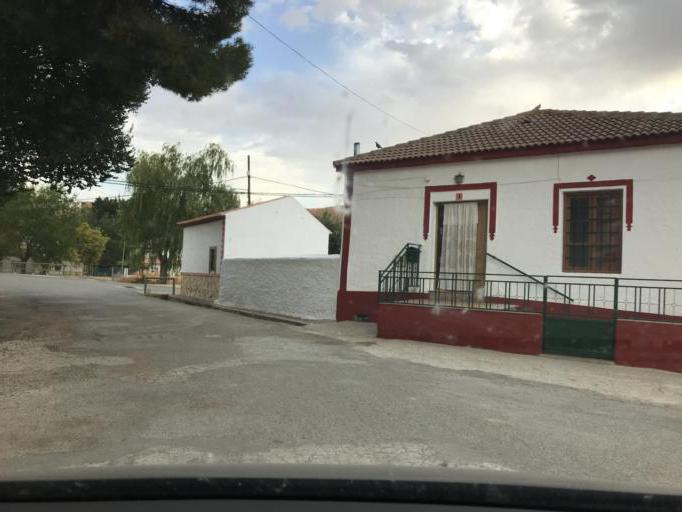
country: ES
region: Andalusia
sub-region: Provincia de Granada
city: Villanueva de las Torres
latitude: 37.4795
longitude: -3.0432
